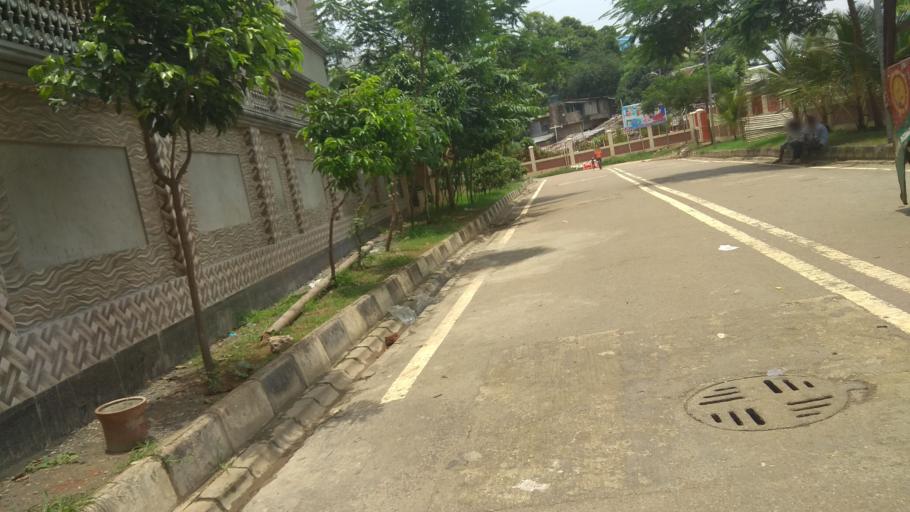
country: BD
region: Dhaka
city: Tungi
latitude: 23.8169
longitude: 90.3587
